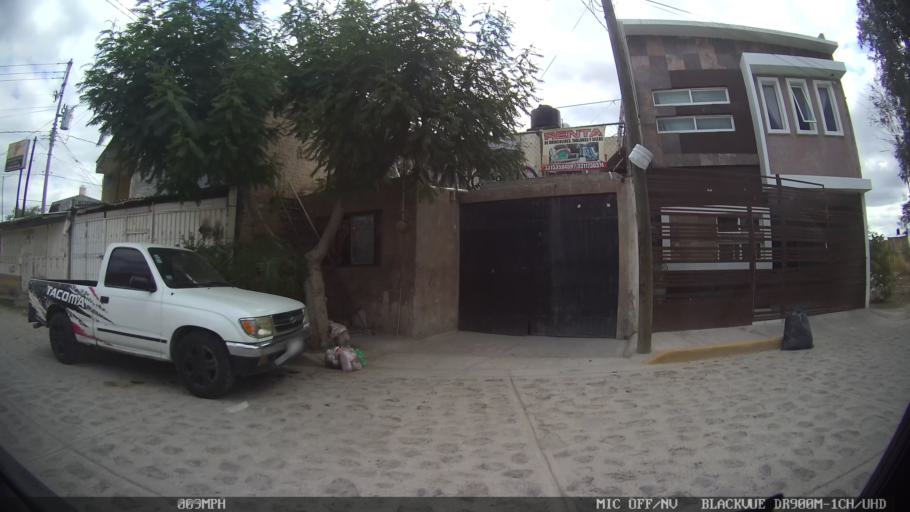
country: MX
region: Jalisco
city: Tlaquepaque
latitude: 20.6710
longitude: -103.2552
